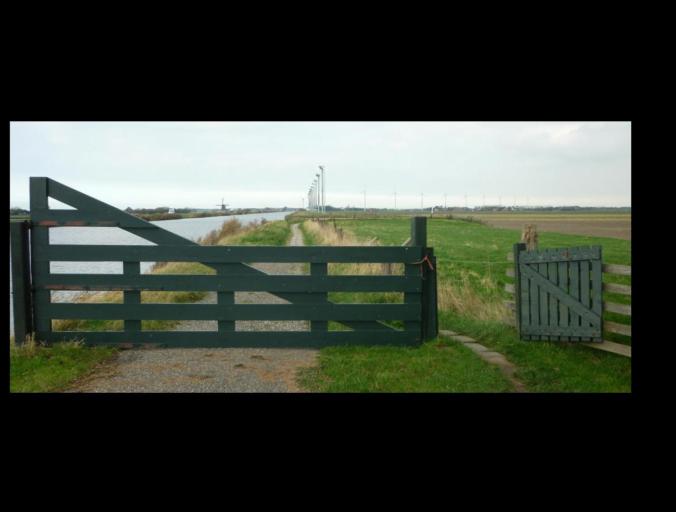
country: NL
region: North Holland
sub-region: Gemeente Schagen
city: Harenkarspel
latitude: 52.7365
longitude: 4.6882
